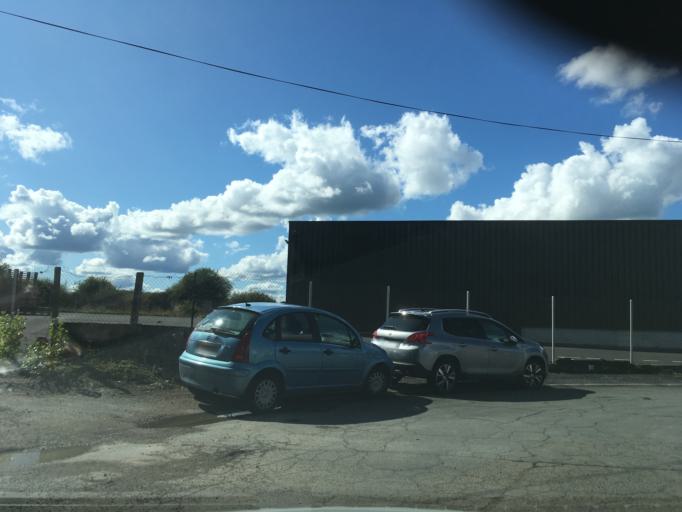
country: FR
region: Limousin
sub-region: Departement de la Correze
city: Saint-Pantaleon-de-Larche
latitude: 45.1494
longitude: 1.4777
